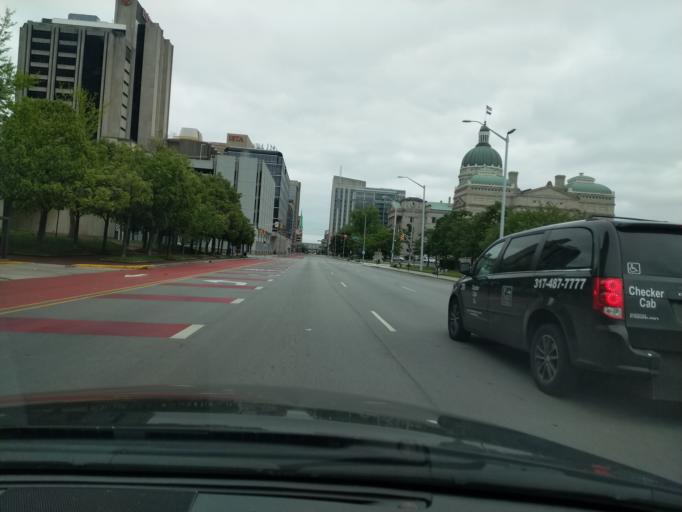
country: US
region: Indiana
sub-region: Marion County
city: Indianapolis
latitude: 39.7709
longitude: -86.1616
